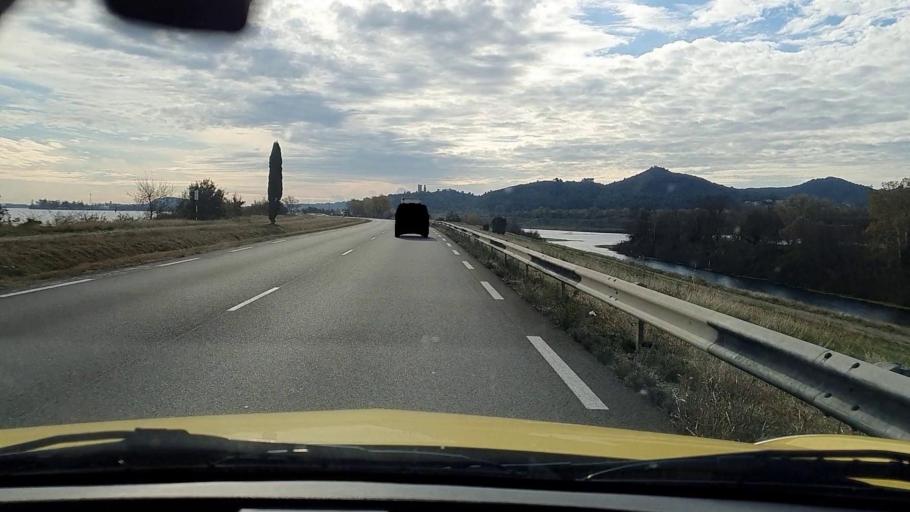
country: FR
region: Languedoc-Roussillon
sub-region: Departement du Gard
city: Vallabregues
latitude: 43.8551
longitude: 4.6172
